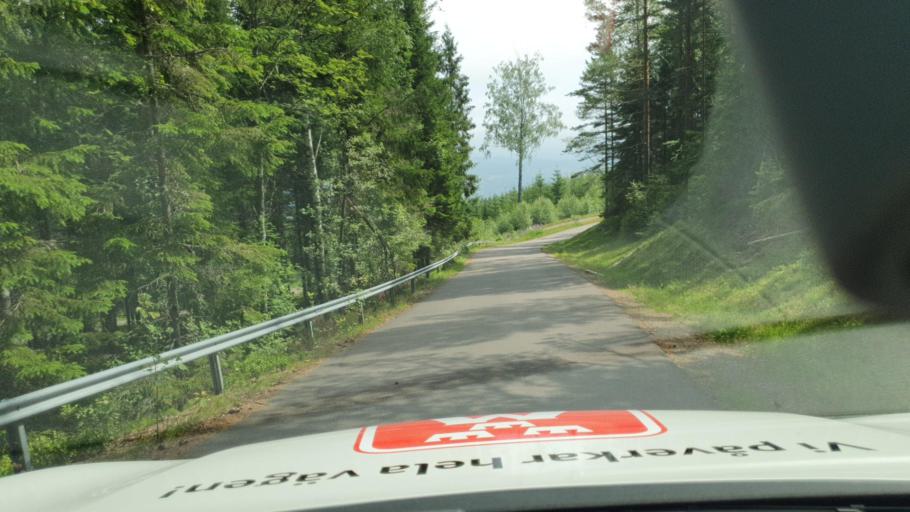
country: SE
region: Vaermland
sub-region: Sunne Kommun
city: Sunne
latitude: 59.9806
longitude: 13.0896
